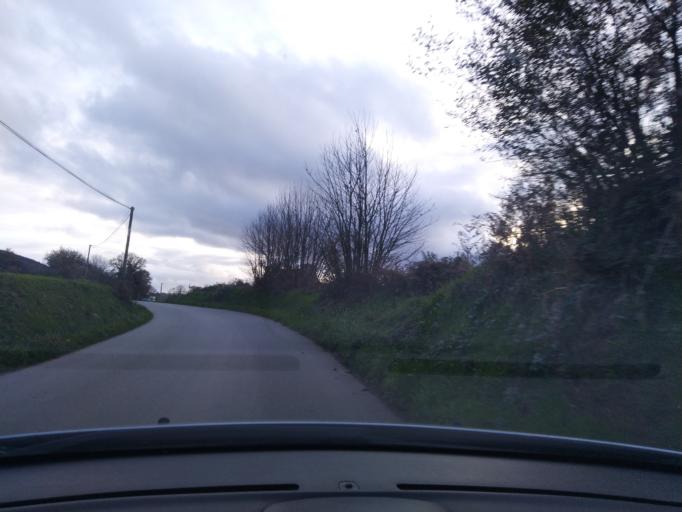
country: FR
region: Brittany
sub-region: Departement du Finistere
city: Guerlesquin
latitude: 48.5594
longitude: -3.6177
